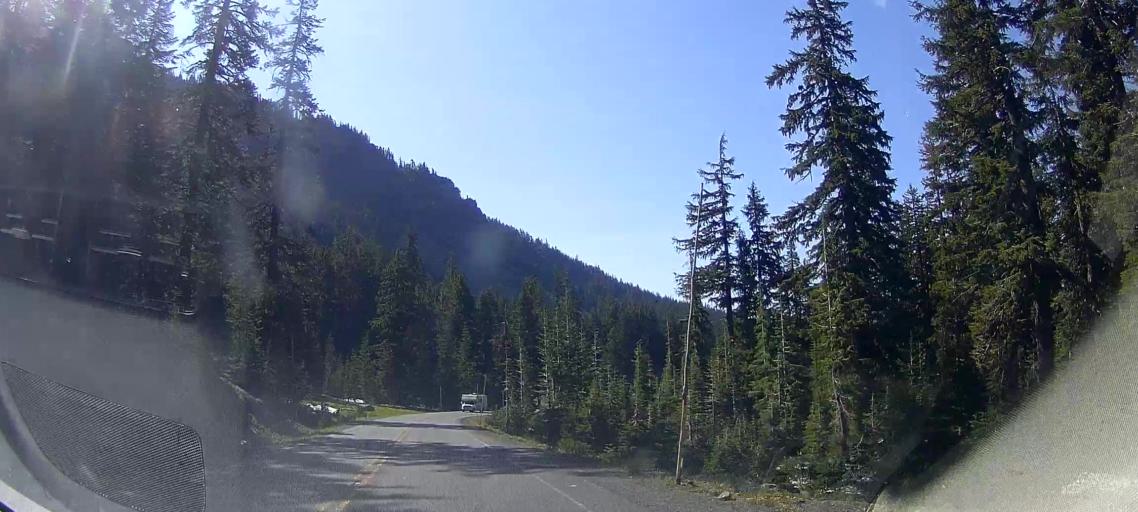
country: US
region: Oregon
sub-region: Jackson County
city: Shady Cove
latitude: 42.9027
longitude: -122.1344
